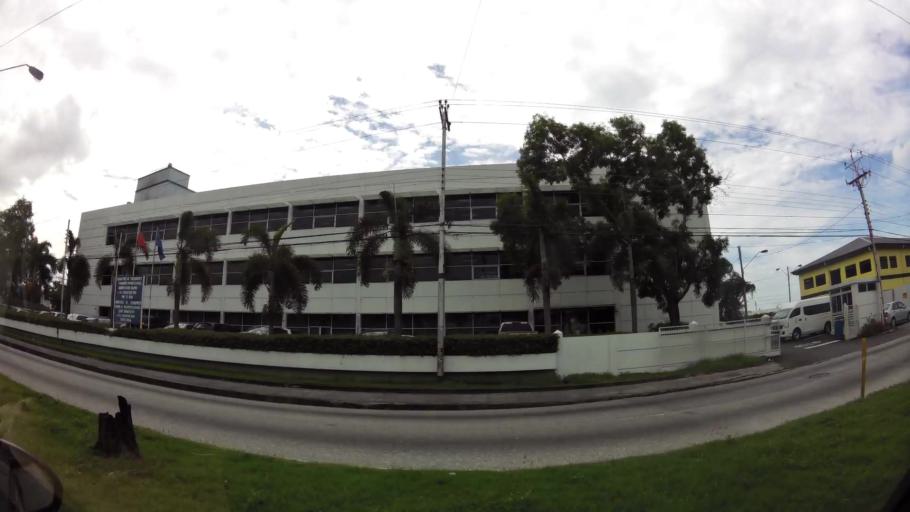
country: TT
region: City of Port of Spain
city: Port-of-Spain
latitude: 10.6602
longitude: -61.5264
